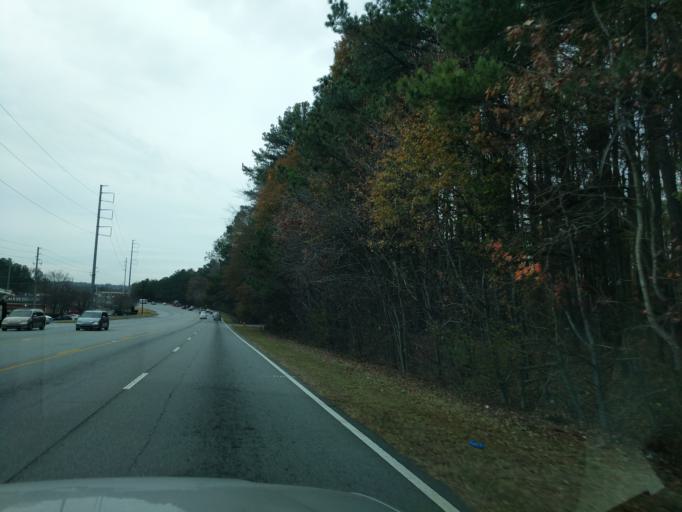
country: US
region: Georgia
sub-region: Gwinnett County
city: Duluth
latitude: 34.0028
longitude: -84.1642
